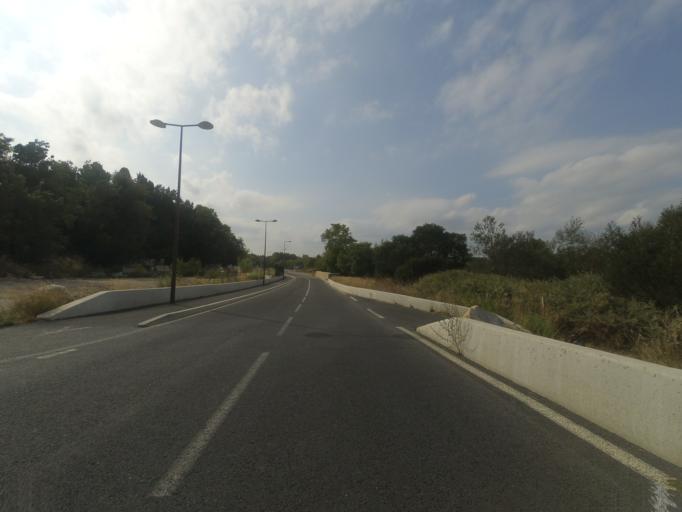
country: FR
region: Languedoc-Roussillon
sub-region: Departement des Pyrenees-Orientales
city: Le Soler
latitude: 42.6838
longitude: 2.7928
